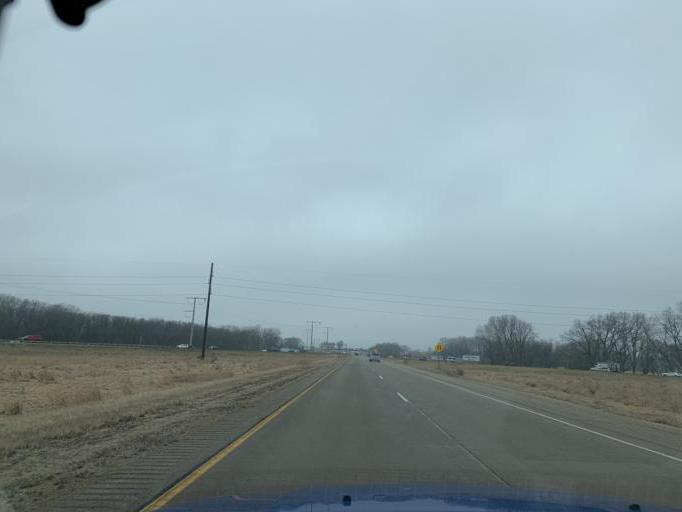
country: US
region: Wisconsin
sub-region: Dane County
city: McFarland
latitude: 43.0471
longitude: -89.2802
